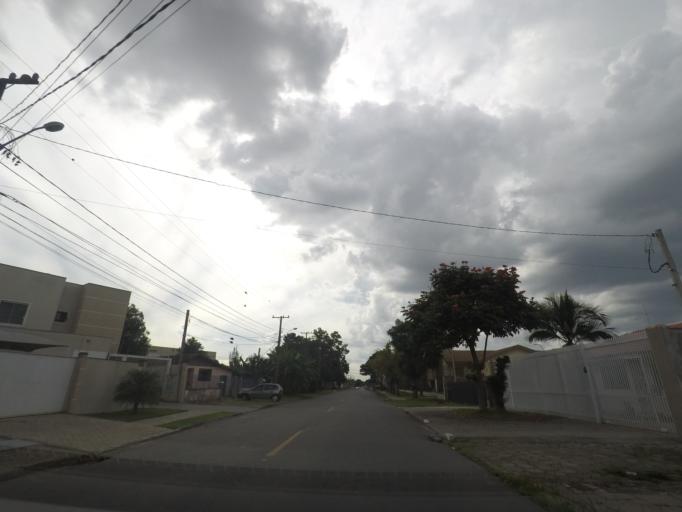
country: BR
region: Parana
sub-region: Sao Jose Dos Pinhais
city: Sao Jose dos Pinhais
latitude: -25.4907
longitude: -49.2454
